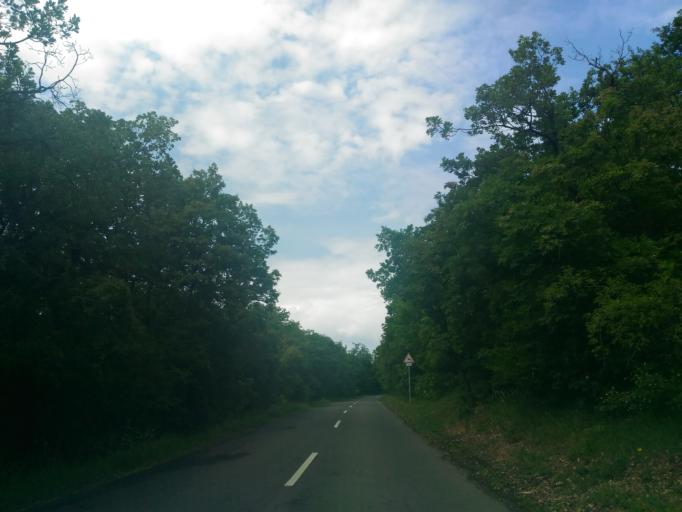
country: HU
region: Baranya
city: Pecs
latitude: 46.0981
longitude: 18.2241
